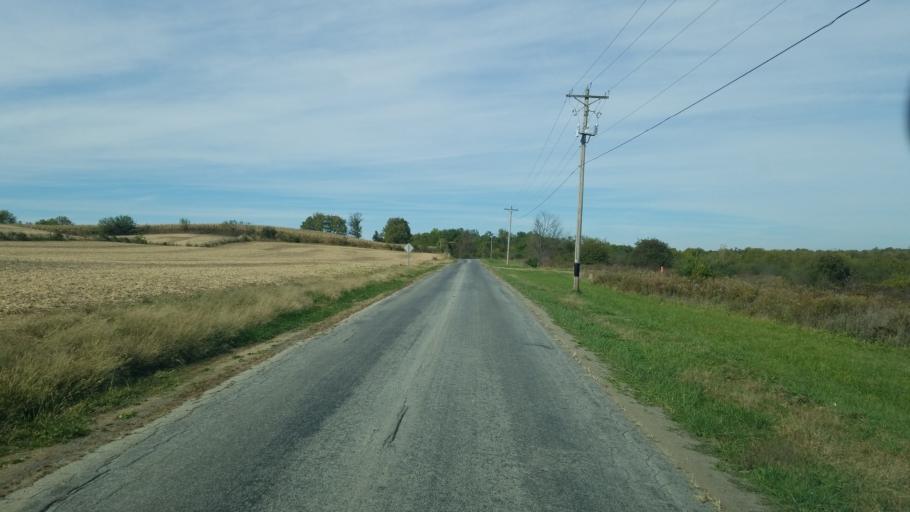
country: US
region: Ohio
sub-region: Highland County
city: Greenfield
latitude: 39.3085
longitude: -83.4623
